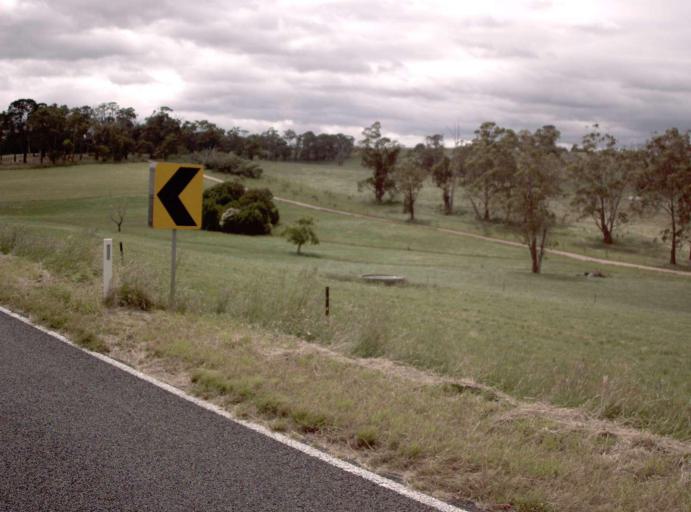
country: AU
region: Victoria
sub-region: Latrobe
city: Moe
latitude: -38.0816
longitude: 146.1666
